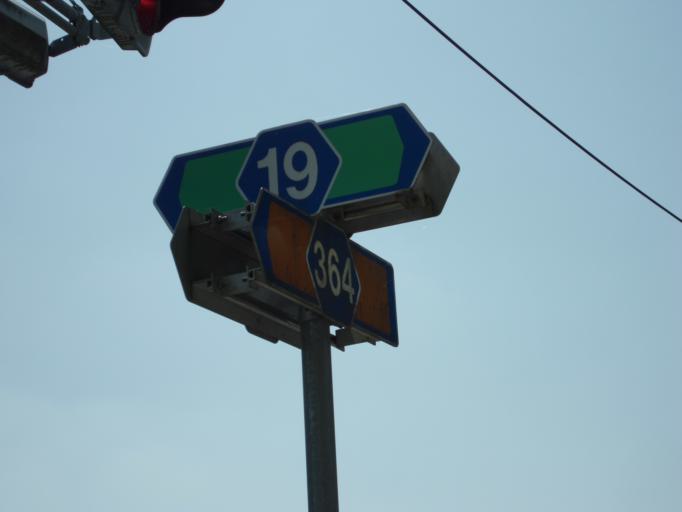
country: JP
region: Kyoto
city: Kameoka
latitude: 35.1544
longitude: 135.5137
